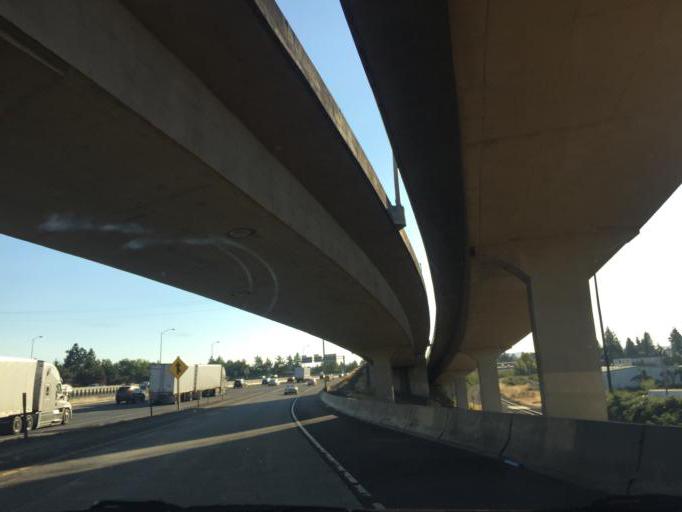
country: US
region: Oregon
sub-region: Multnomah County
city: Lents
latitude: 45.5323
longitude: -122.5668
